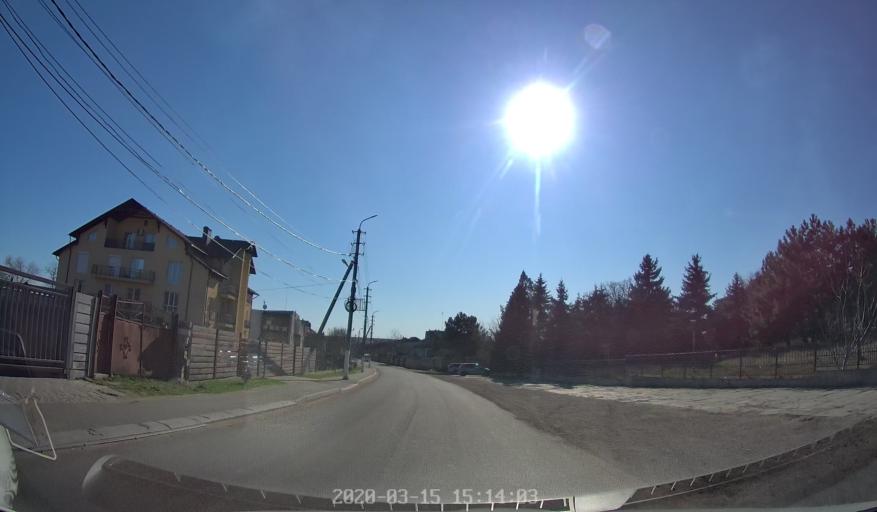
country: MD
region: Chisinau
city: Cricova
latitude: 47.2482
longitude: 28.7684
